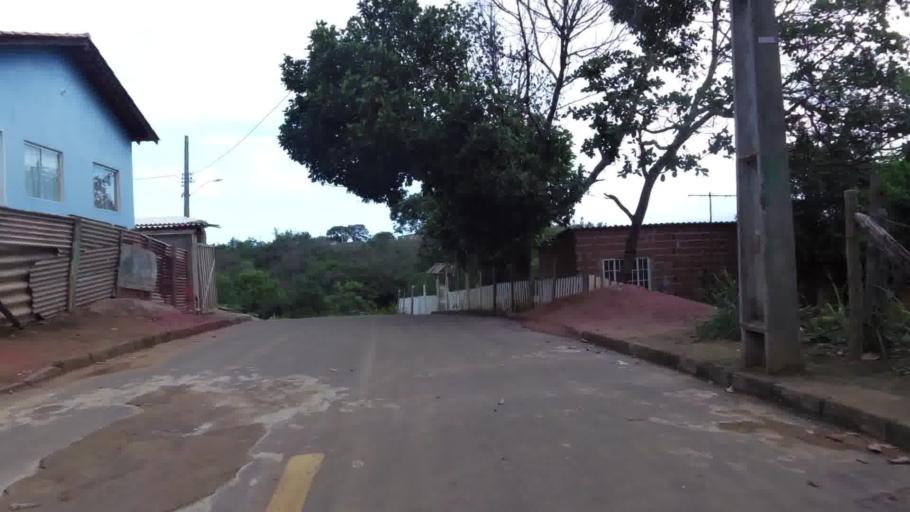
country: BR
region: Espirito Santo
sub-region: Piuma
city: Piuma
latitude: -20.7976
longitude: -40.6463
